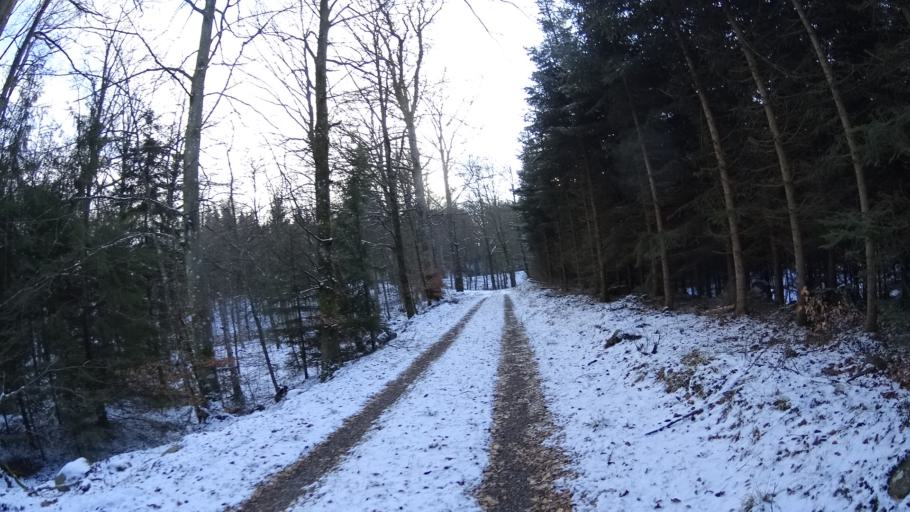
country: SE
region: Skane
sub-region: Hoors Kommun
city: Hoeoer
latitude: 55.9926
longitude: 13.5538
